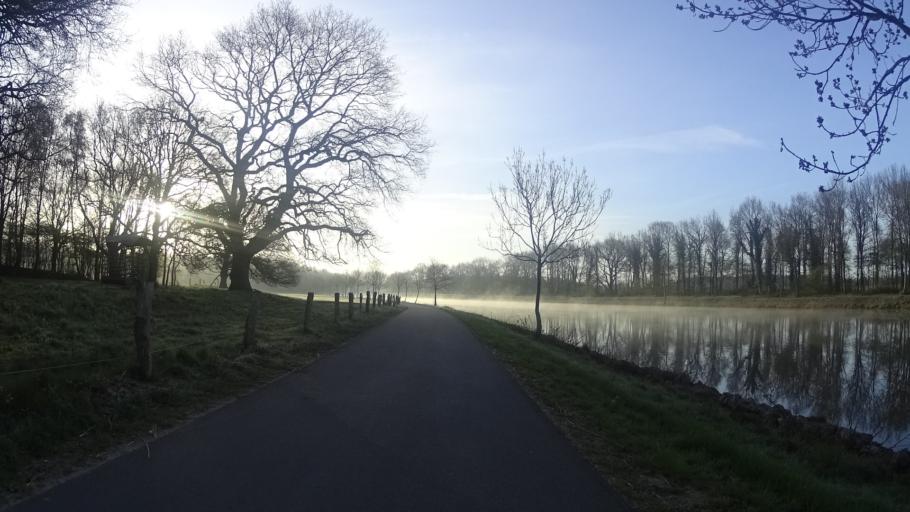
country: DE
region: Lower Saxony
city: Sustrum
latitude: 52.9141
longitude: 7.3031
